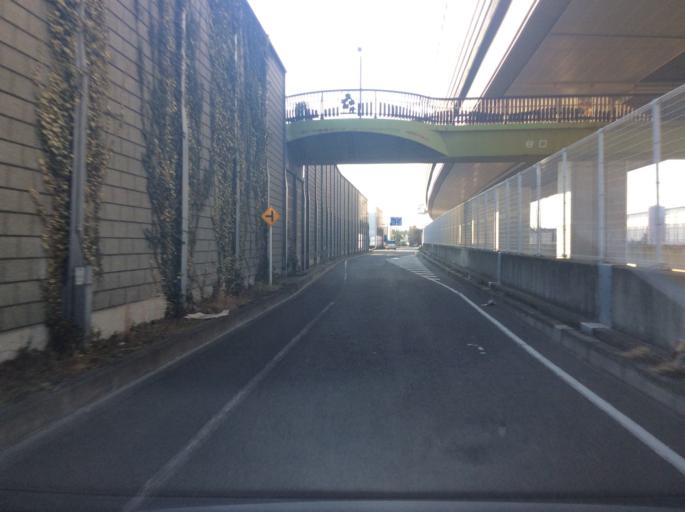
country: JP
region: Saitama
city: Yashio-shi
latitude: 35.8269
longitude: 139.8698
